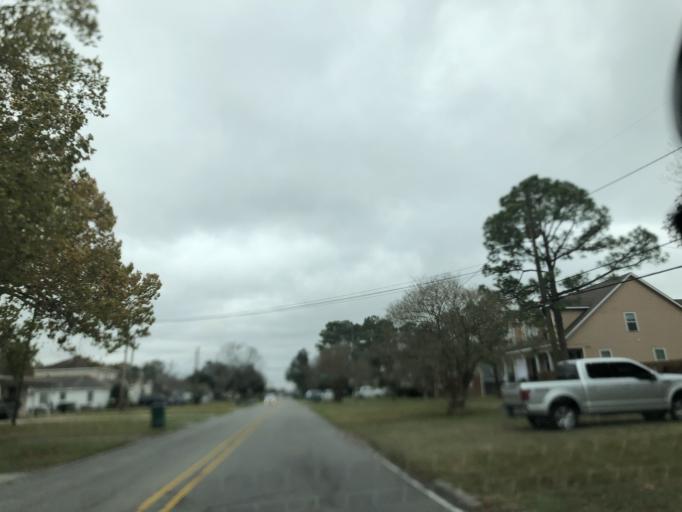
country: US
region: Louisiana
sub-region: Jefferson Parish
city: Metairie Terrace
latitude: 29.9805
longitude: -90.1604
